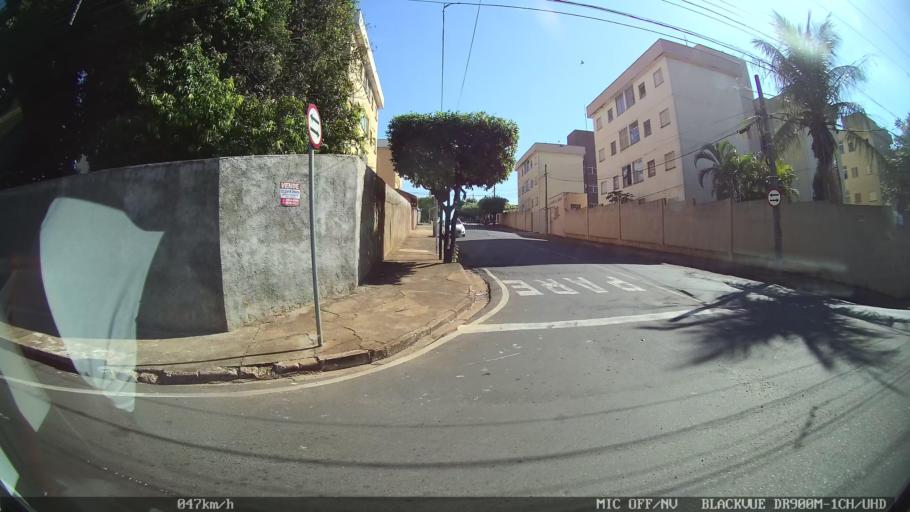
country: BR
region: Sao Paulo
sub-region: Sao Jose Do Rio Preto
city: Sao Jose do Rio Preto
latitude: -20.8007
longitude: -49.4066
